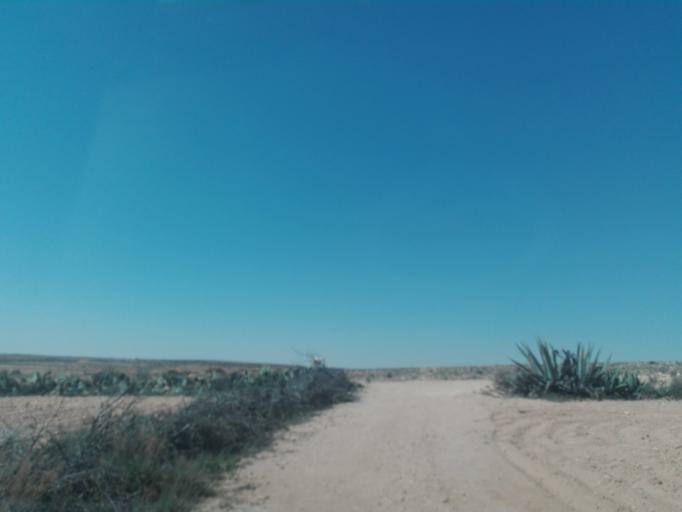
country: TN
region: Safaqis
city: Bi'r `Ali Bin Khalifah
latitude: 34.7936
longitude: 10.2812
